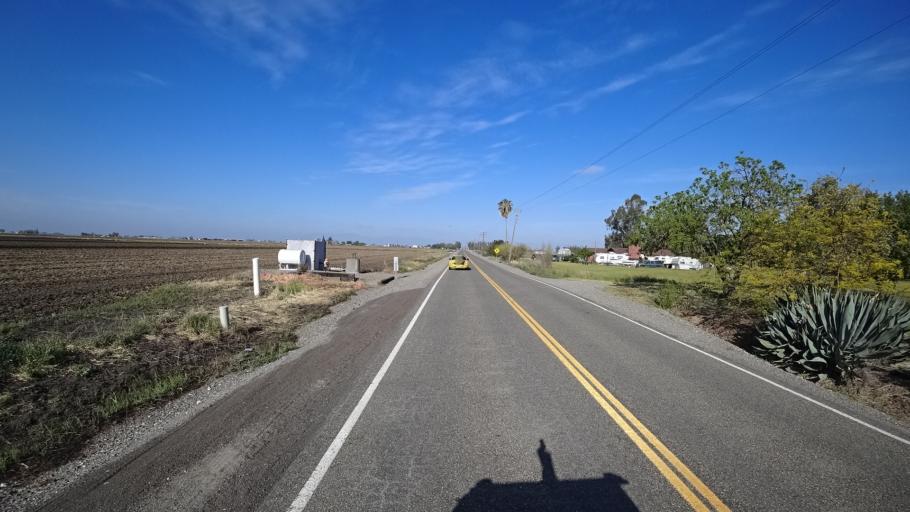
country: US
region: California
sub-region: Glenn County
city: Willows
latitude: 39.5826
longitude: -122.0532
